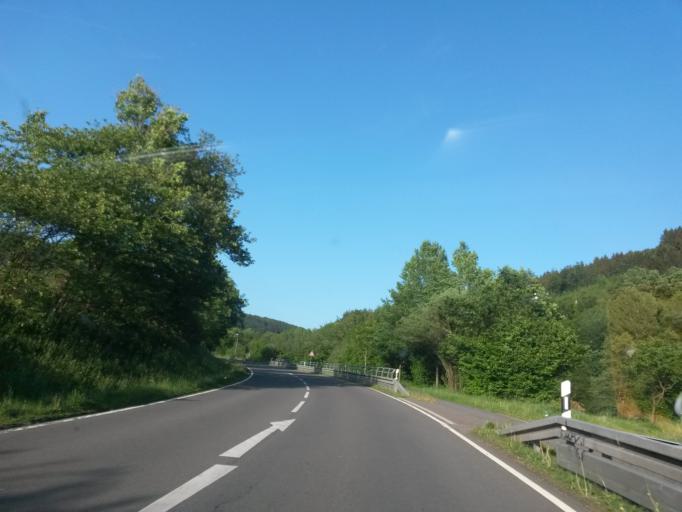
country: DE
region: North Rhine-Westphalia
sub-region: Regierungsbezirk Arnsberg
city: Drolshagen
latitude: 51.0410
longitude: 7.7165
